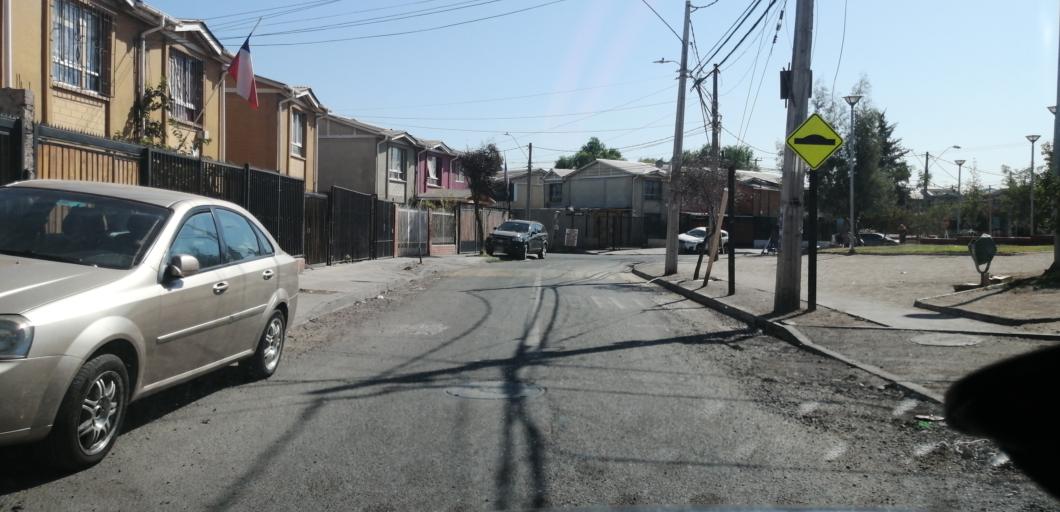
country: CL
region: Santiago Metropolitan
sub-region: Provincia de Santiago
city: Lo Prado
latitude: -33.4392
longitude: -70.7711
